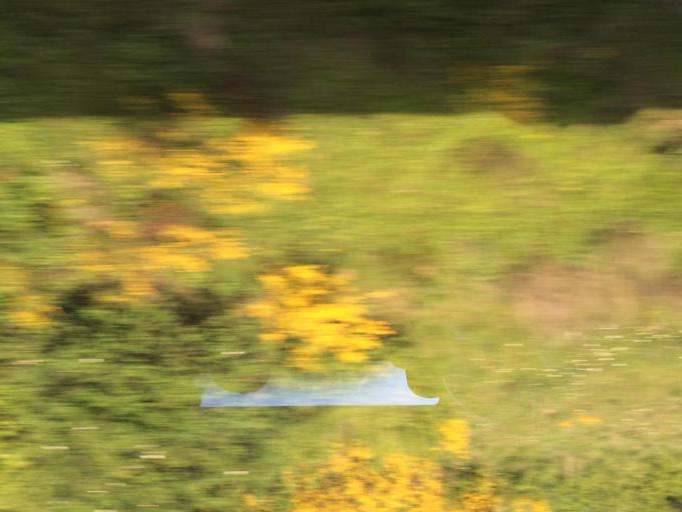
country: DE
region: North Rhine-Westphalia
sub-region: Regierungsbezirk Koln
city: Konigswinter
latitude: 50.7154
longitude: 7.2407
